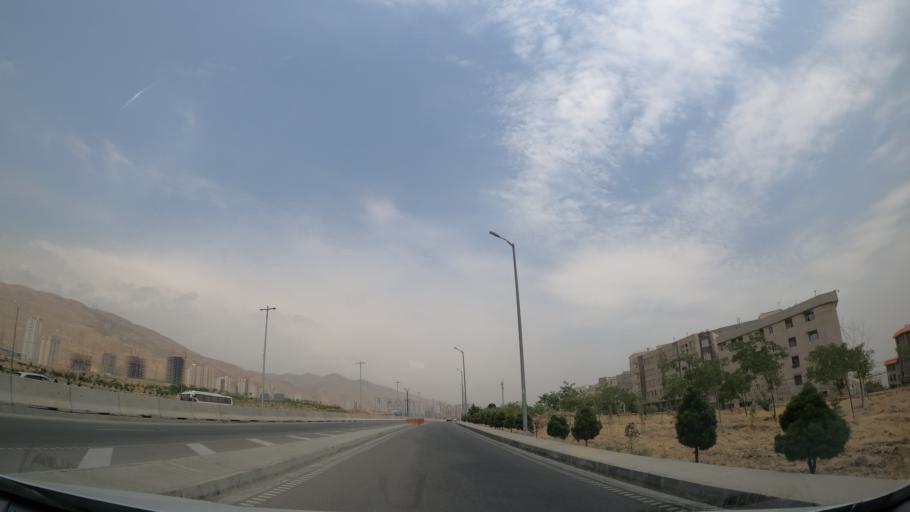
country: IR
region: Tehran
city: Shahr-e Qods
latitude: 35.7433
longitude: 51.1283
